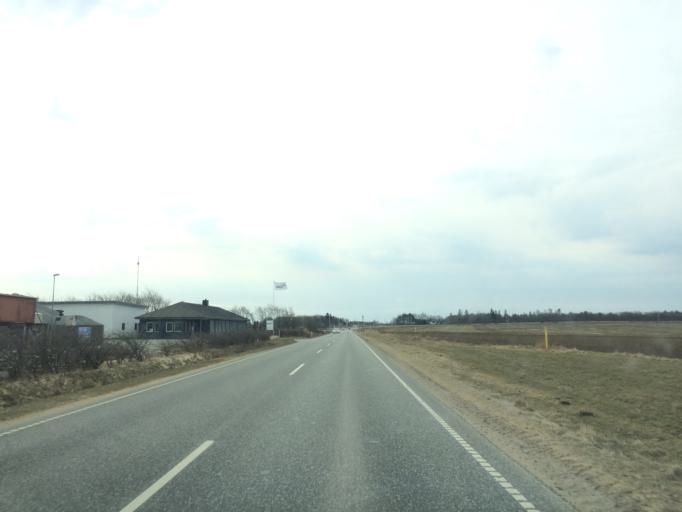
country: DK
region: Central Jutland
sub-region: Ringkobing-Skjern Kommune
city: Videbaek
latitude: 56.0924
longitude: 8.5075
